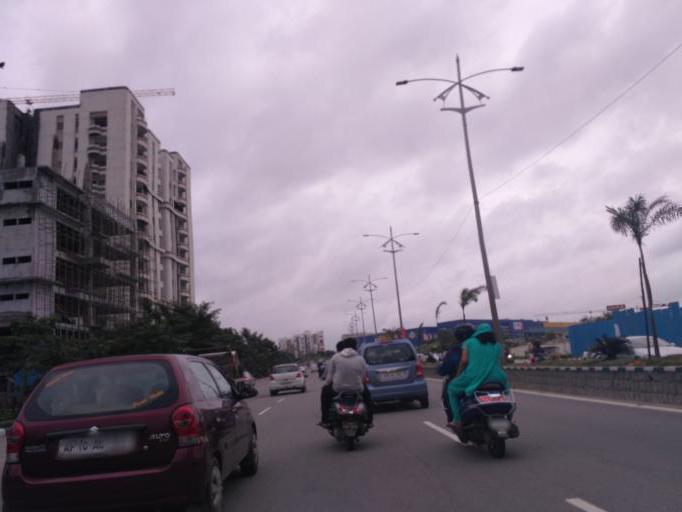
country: IN
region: Telangana
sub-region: Rangareddi
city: Kukatpalli
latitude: 17.4340
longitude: 78.3745
